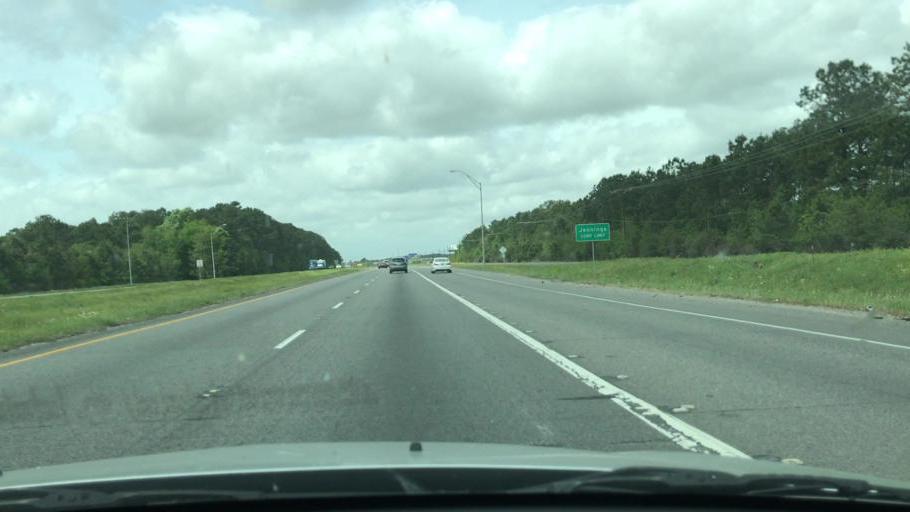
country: US
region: Louisiana
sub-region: Jefferson Davis Parish
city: Jennings
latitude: 30.2436
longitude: -92.6337
